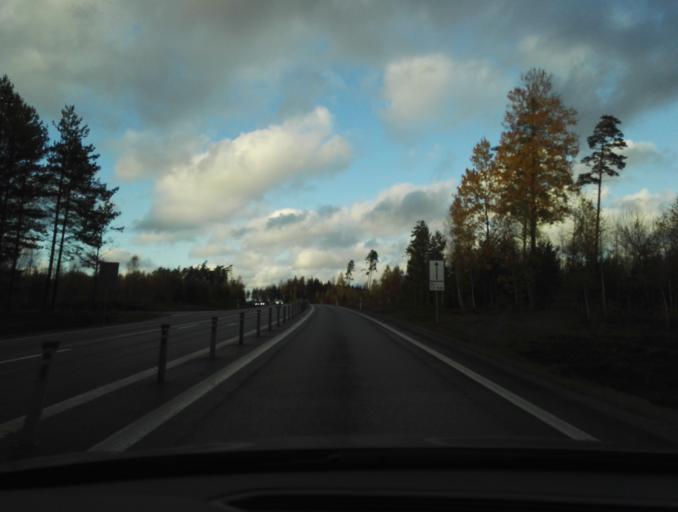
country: SE
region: Kronoberg
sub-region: Vaxjo Kommun
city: Vaexjoe
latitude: 56.9028
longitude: 14.7294
